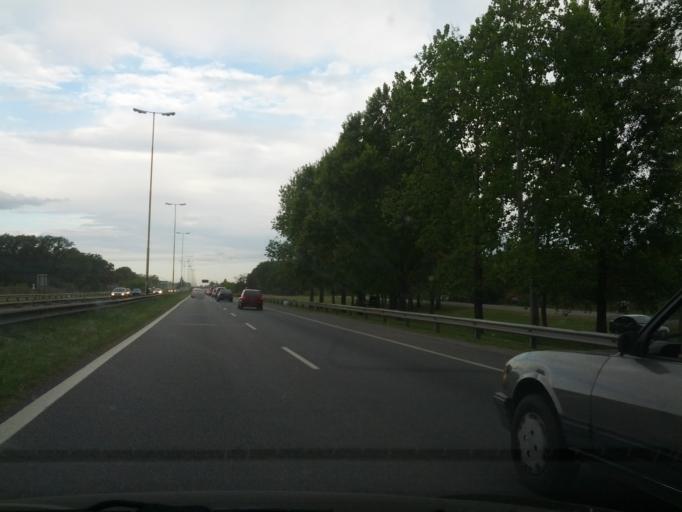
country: AR
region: Buenos Aires
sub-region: Partido de General Rodriguez
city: General Rodriguez
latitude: -34.5866
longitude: -58.9781
